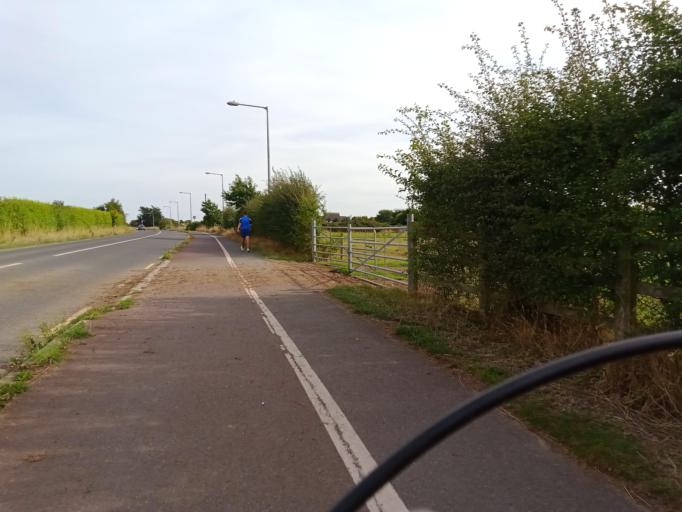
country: IE
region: Munster
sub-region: Waterford
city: Dungarvan
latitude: 52.0959
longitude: -7.5587
